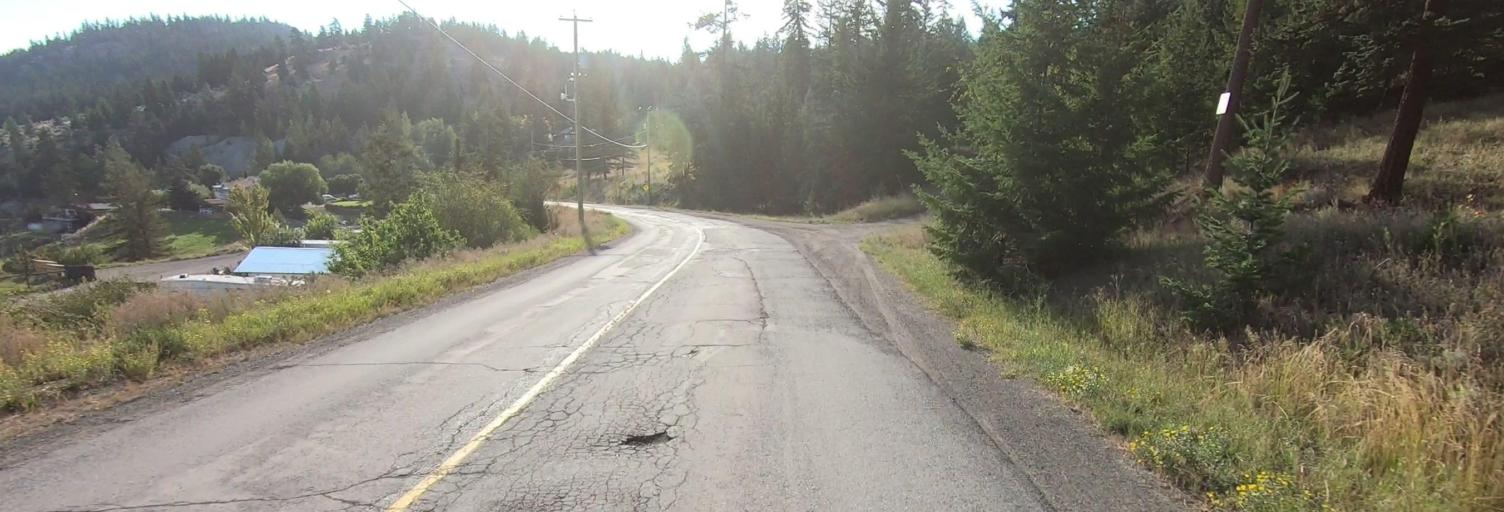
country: CA
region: British Columbia
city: Kamloops
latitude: 50.6556
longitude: -120.4415
